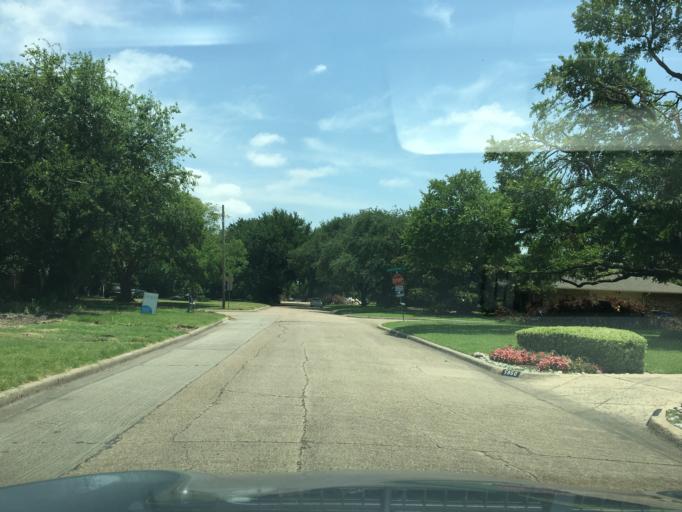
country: US
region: Texas
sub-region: Dallas County
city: Addison
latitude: 32.9163
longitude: -96.8081
